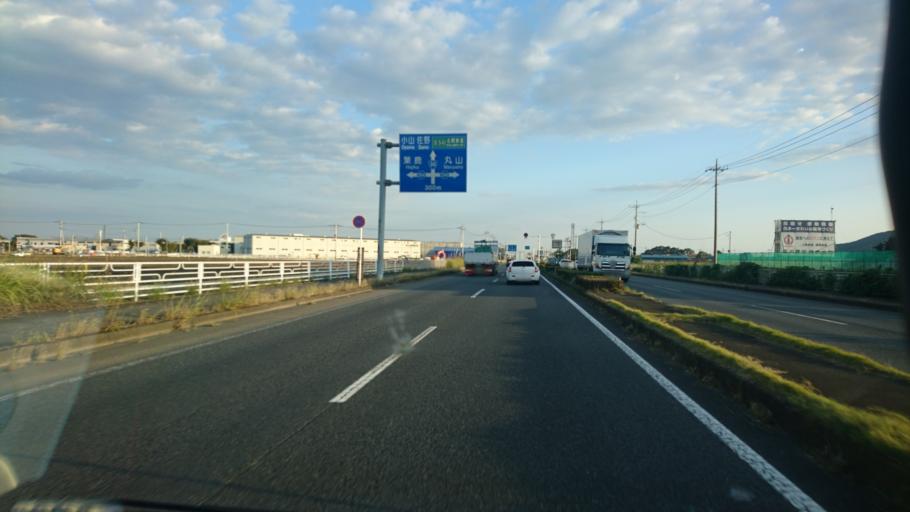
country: JP
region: Gunma
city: Ota
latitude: 36.3493
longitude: 139.3792
